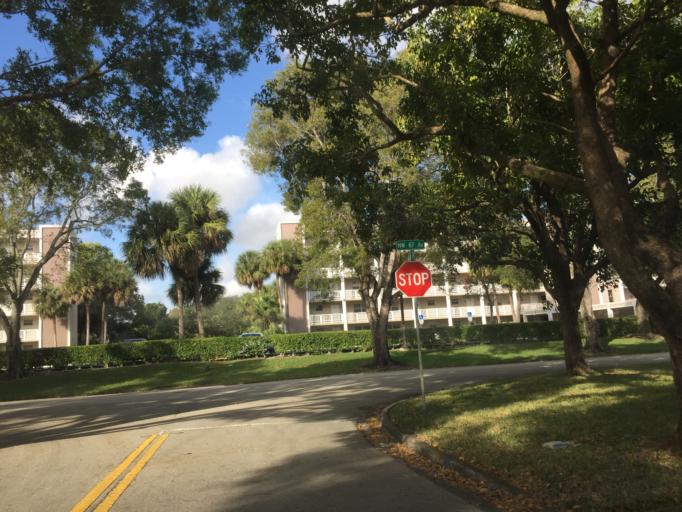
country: US
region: Florida
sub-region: Broward County
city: North Lauderdale
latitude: 26.2449
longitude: -80.2411
